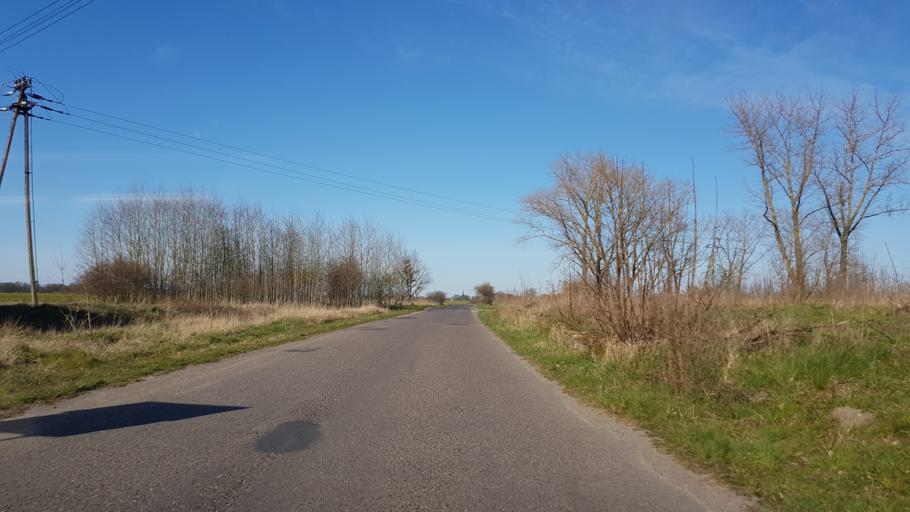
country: PL
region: West Pomeranian Voivodeship
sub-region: Powiat goleniowski
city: Maszewo
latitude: 53.4241
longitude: 15.0545
